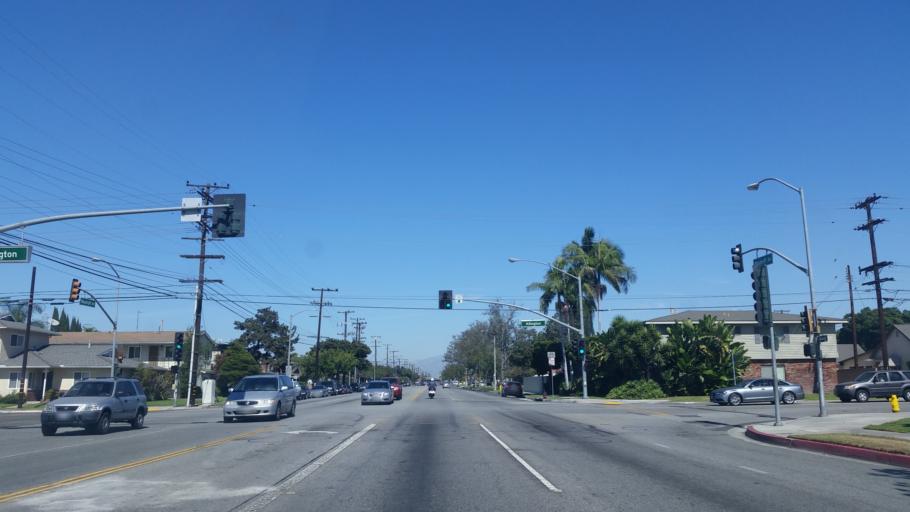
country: US
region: California
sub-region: Los Angeles County
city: Bellflower
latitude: 33.8651
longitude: -118.1171
